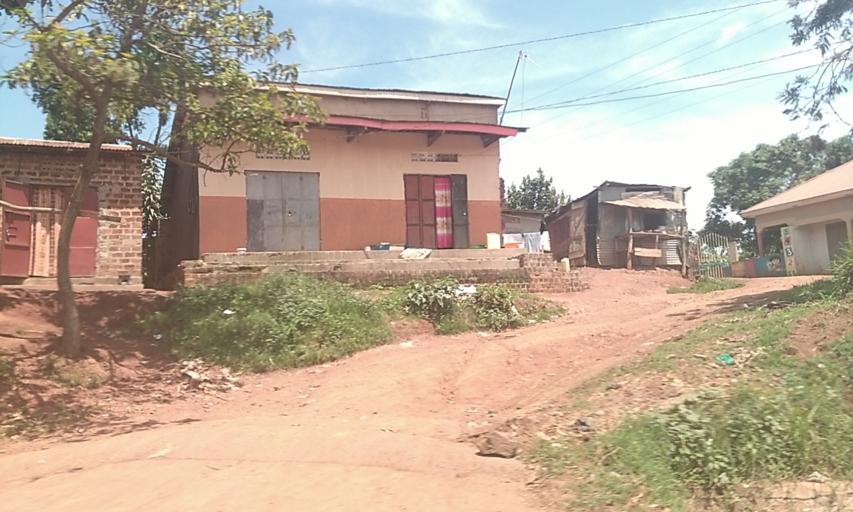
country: UG
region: Central Region
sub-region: Wakiso District
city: Wakiso
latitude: 0.4087
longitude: 32.4659
